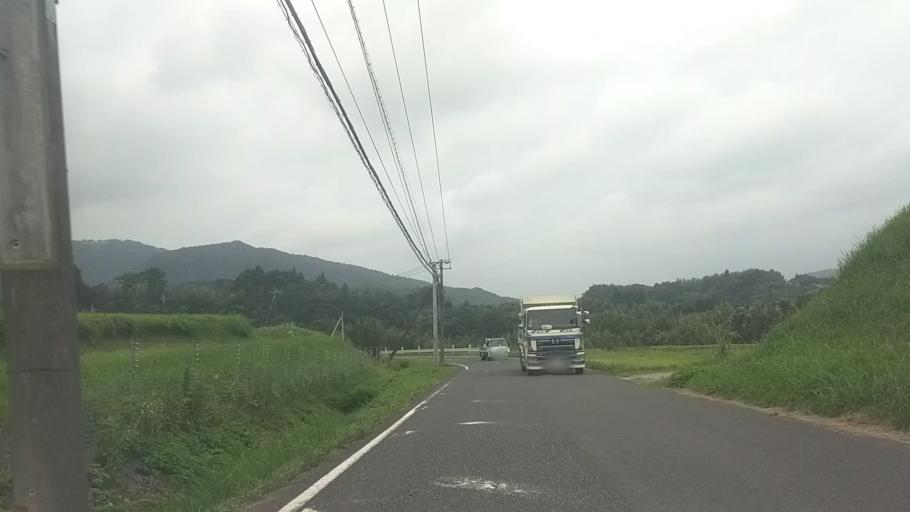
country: JP
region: Chiba
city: Kimitsu
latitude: 35.2432
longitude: 139.9960
